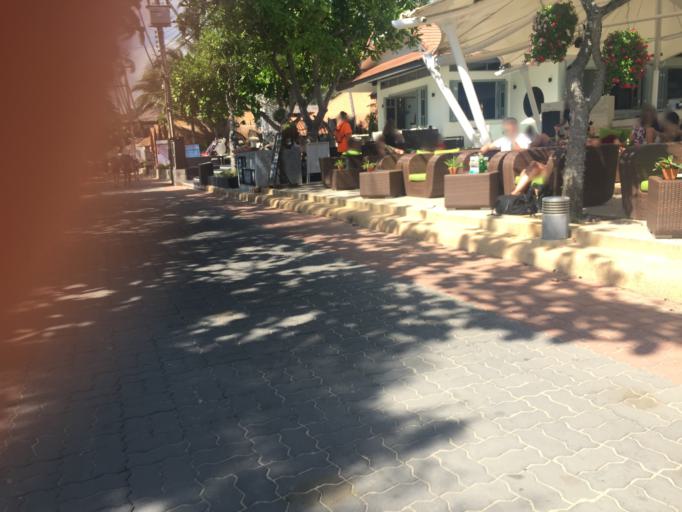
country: TH
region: Phangnga
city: Ban Ao Nang
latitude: 8.0302
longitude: 98.8231
